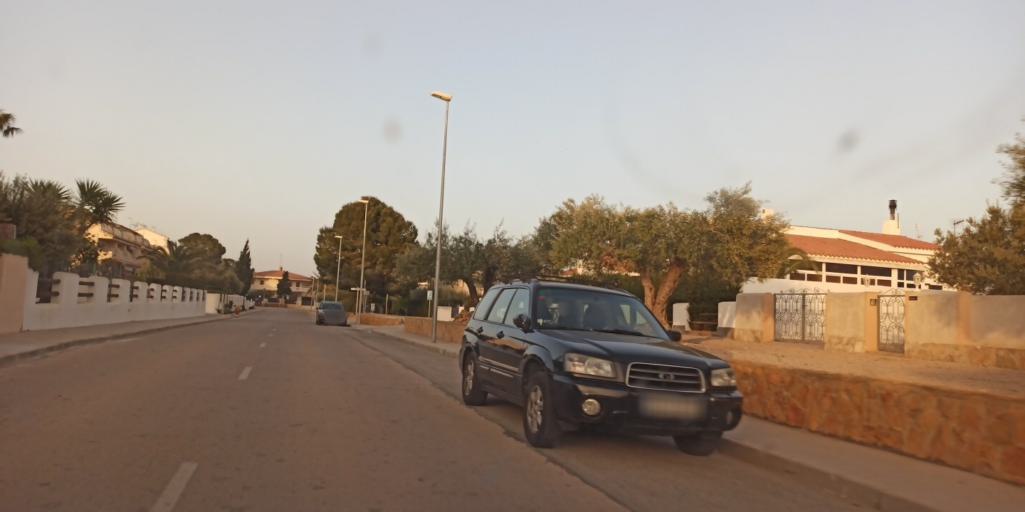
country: ES
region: Catalonia
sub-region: Provincia de Tarragona
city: L'Ampolla
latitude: 40.8220
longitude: 0.7278
